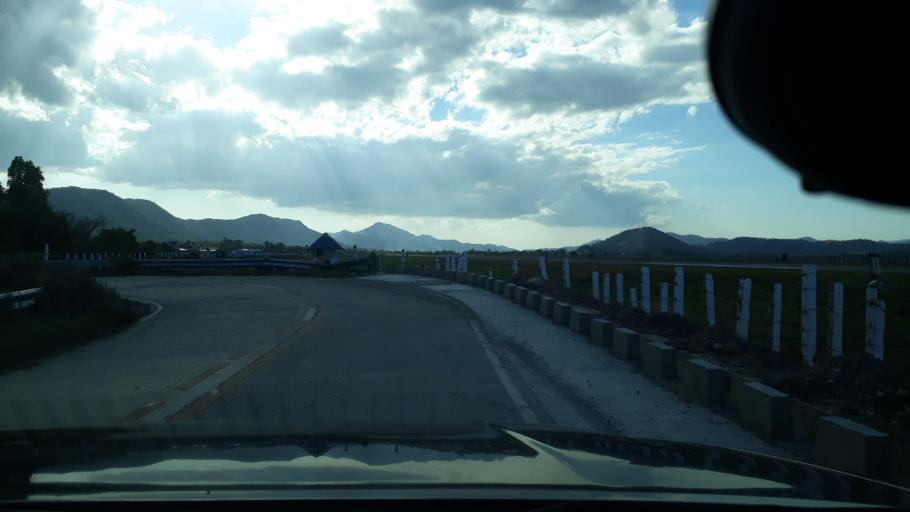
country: PH
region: Mimaropa
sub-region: Province of Palawan
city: Coron
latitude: 12.1217
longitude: 120.1048
